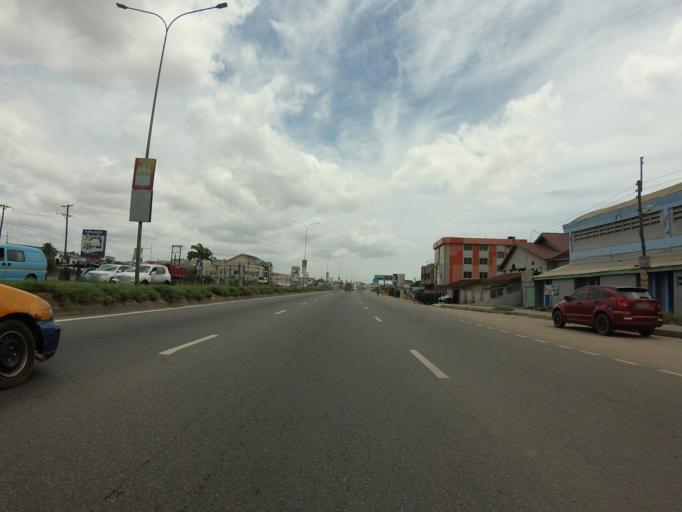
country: GH
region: Greater Accra
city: Gbawe
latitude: 5.5531
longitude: -0.3225
